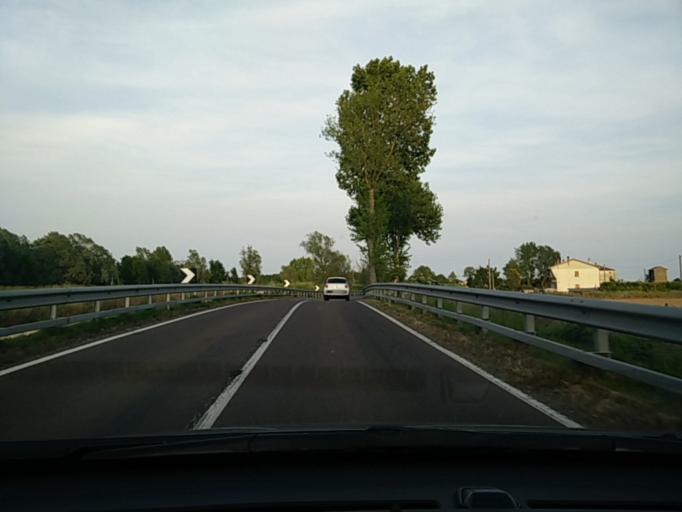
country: IT
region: Veneto
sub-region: Provincia di Venezia
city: Quarto d'Altino
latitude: 45.5628
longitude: 12.4194
